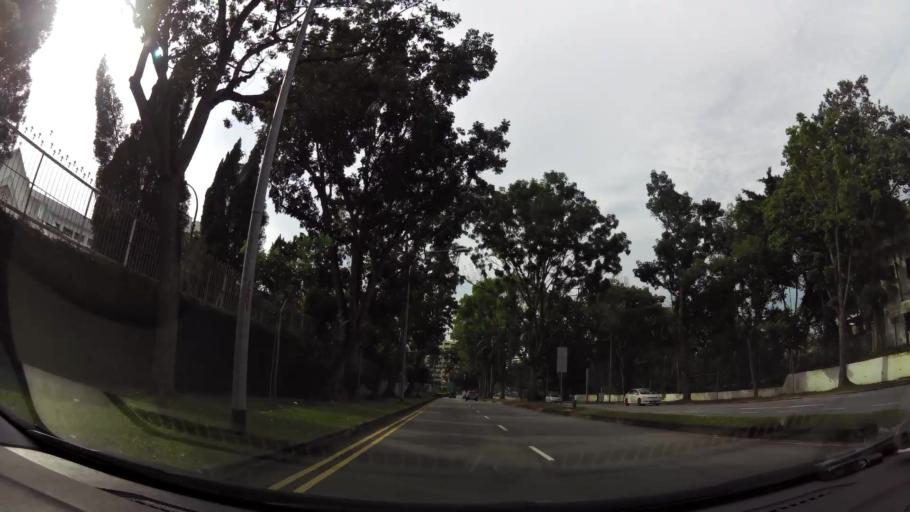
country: SG
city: Singapore
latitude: 1.3739
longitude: 103.8988
